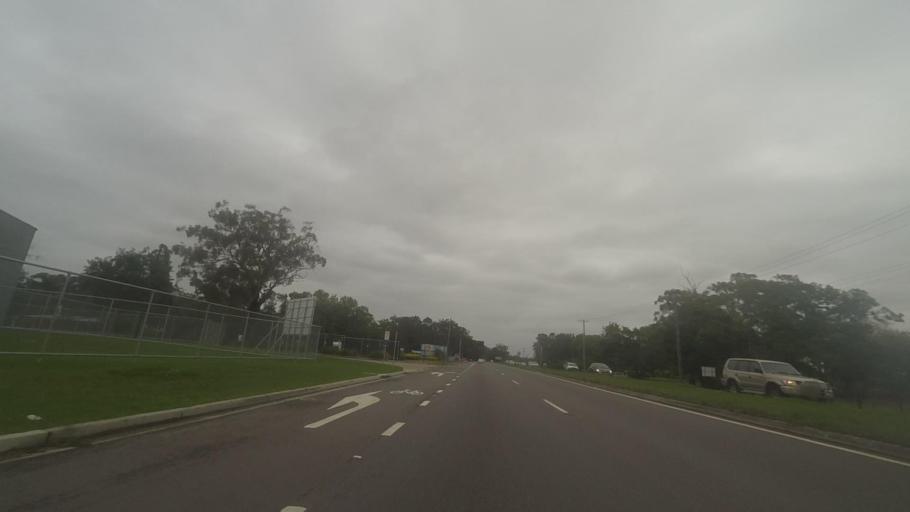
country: AU
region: New South Wales
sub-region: Port Stephens Shire
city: Raymond Terrace
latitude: -32.7927
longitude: 151.7238
